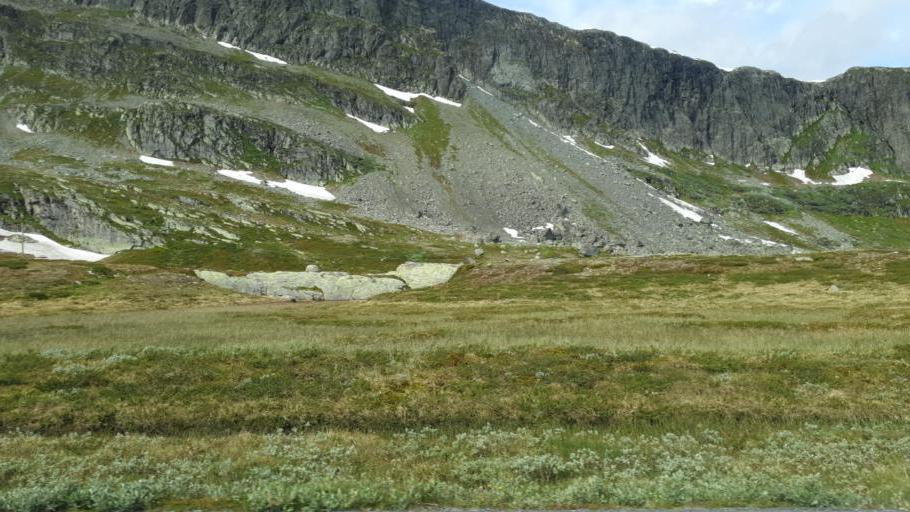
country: NO
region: Oppland
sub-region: Vestre Slidre
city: Slidre
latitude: 61.2964
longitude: 8.8142
